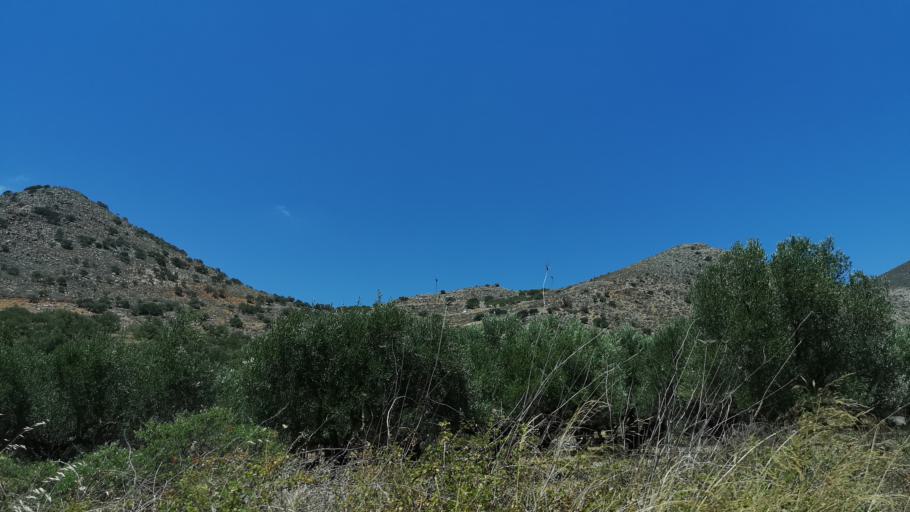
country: GR
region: Crete
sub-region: Nomos Lasithiou
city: Neapoli
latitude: 35.2477
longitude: 25.6286
